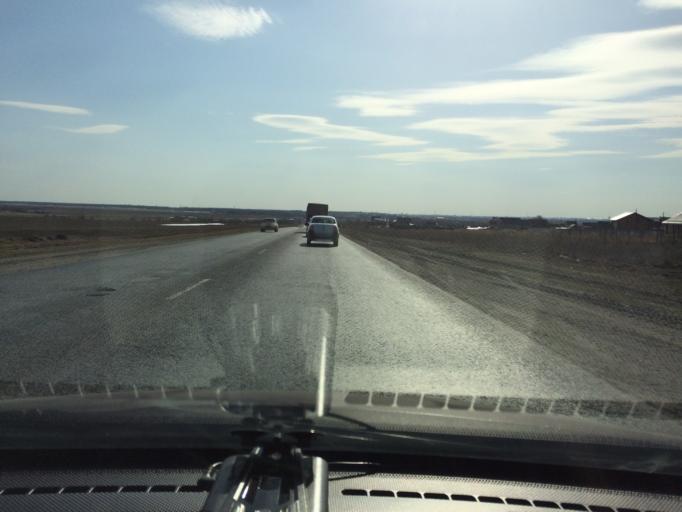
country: RU
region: Mariy-El
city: Yoshkar-Ola
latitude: 56.6954
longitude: 48.0586
